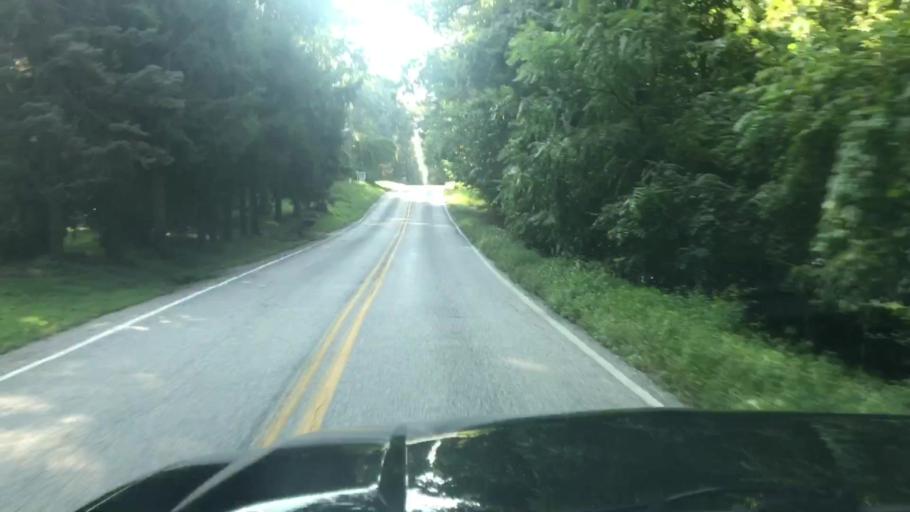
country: US
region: Pennsylvania
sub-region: York County
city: Valley Green
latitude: 40.1536
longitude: -76.8437
